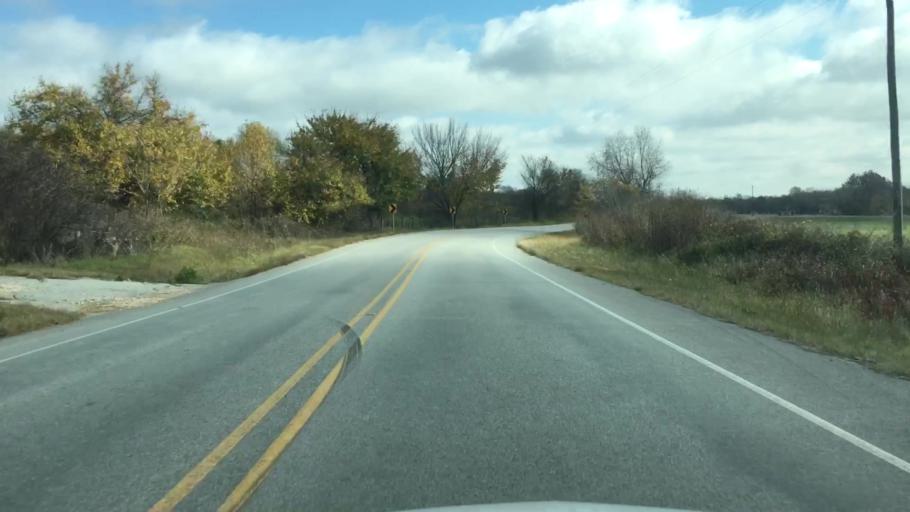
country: US
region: Arkansas
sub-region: Benton County
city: Centerton
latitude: 36.3015
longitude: -94.3100
